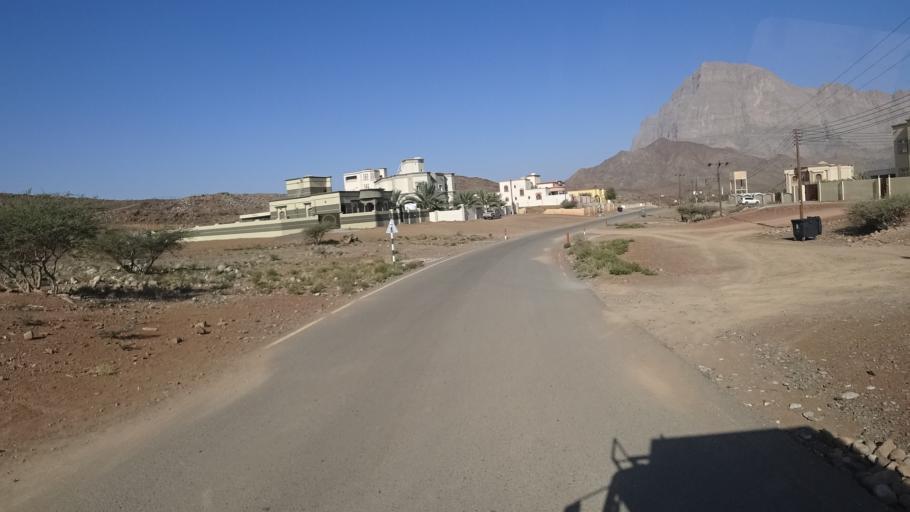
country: OM
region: Muhafazat ad Dakhiliyah
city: Bahla'
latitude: 23.2270
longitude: 57.0482
